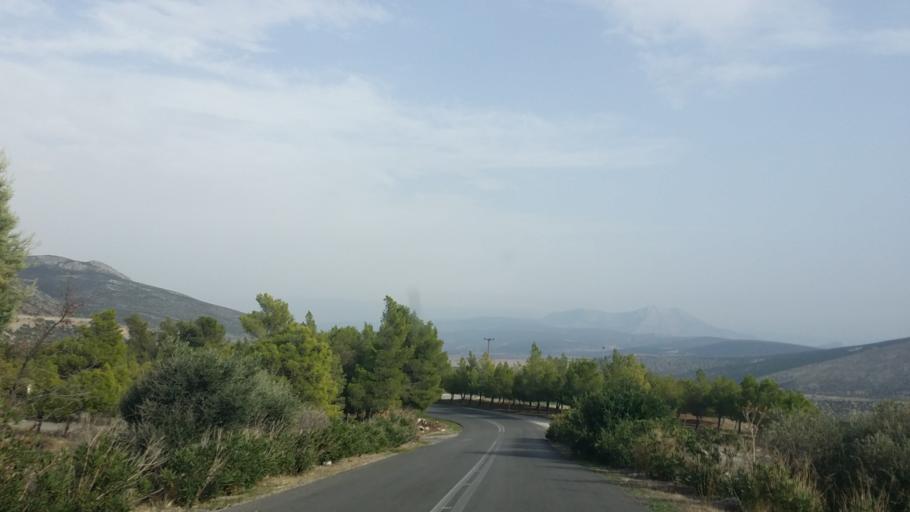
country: GR
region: Central Greece
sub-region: Nomos Voiotias
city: Korini
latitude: 38.2561
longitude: 22.9055
